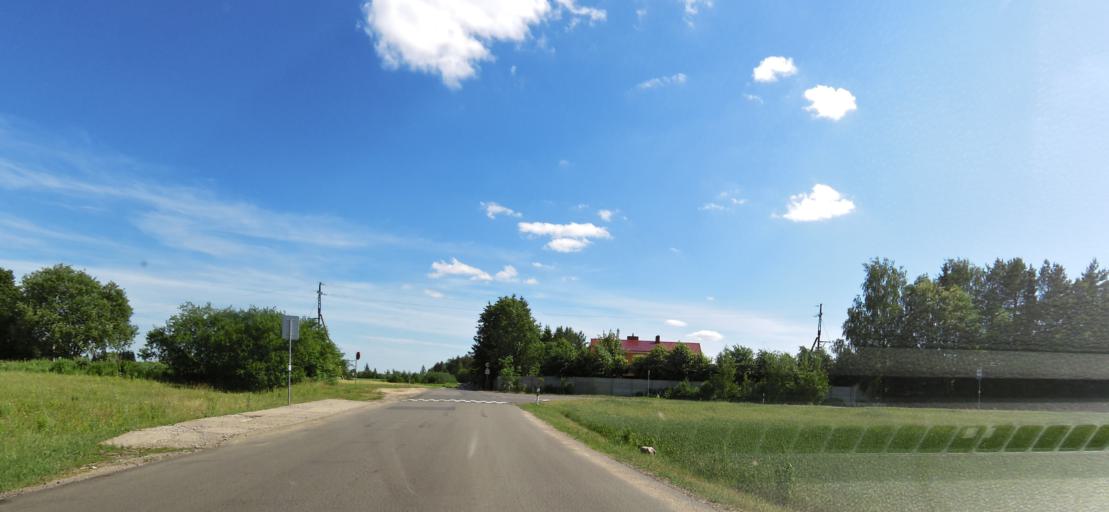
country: LT
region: Vilnius County
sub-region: Vilnius
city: Fabijoniskes
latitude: 54.8067
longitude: 25.3270
